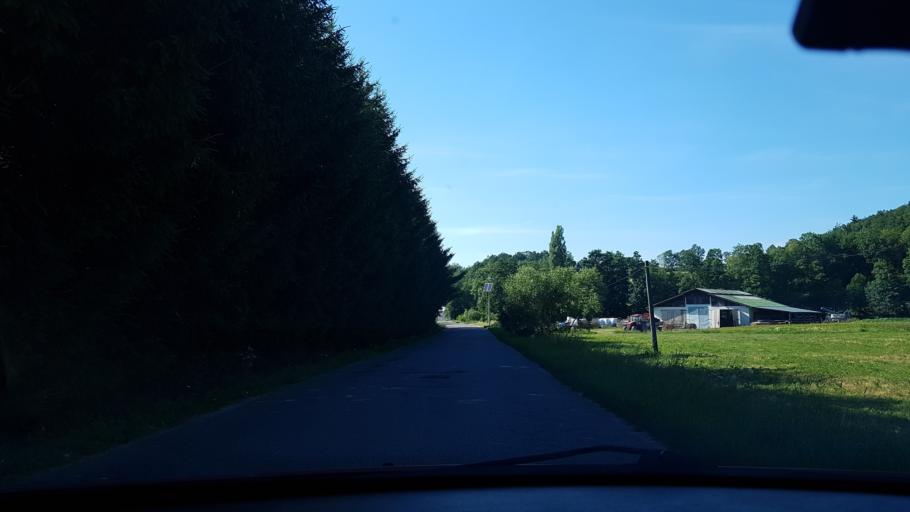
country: PL
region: Lower Silesian Voivodeship
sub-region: Powiat klodzki
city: Bystrzyca Klodzka
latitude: 50.2465
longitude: 16.7040
